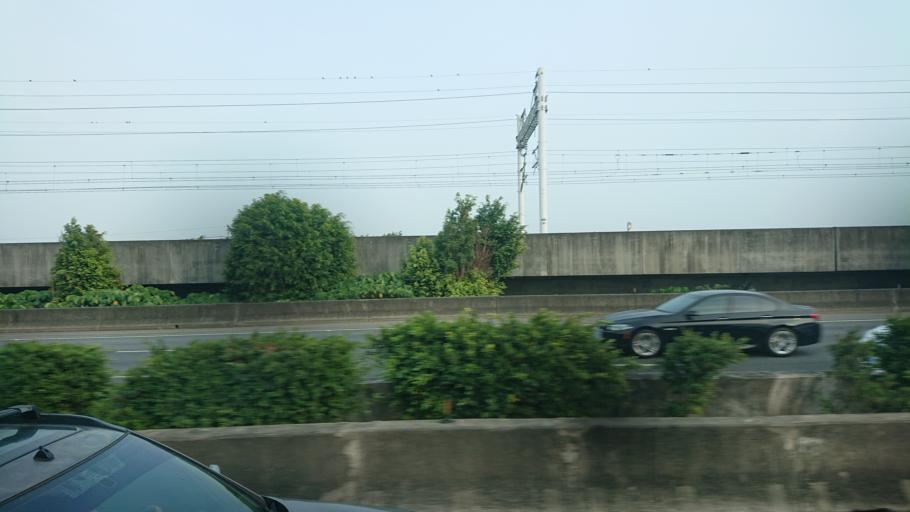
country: TW
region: Taiwan
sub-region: Taichung City
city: Taichung
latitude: 24.1272
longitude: 120.6170
